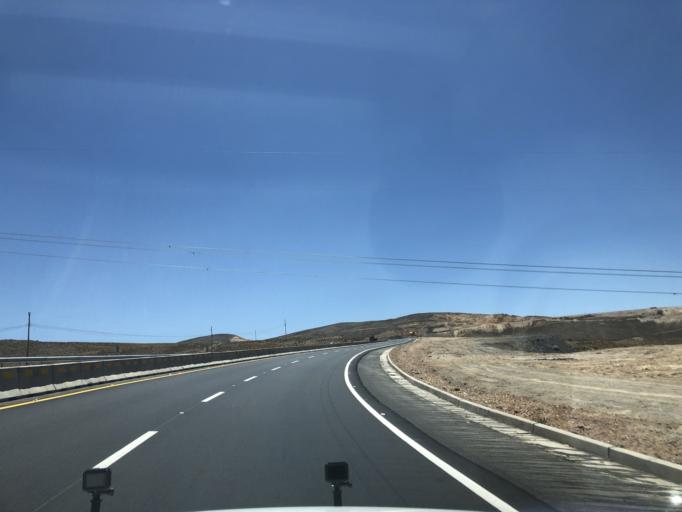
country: BO
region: Cochabamba
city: Colchani
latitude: -17.6842
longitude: -66.7538
